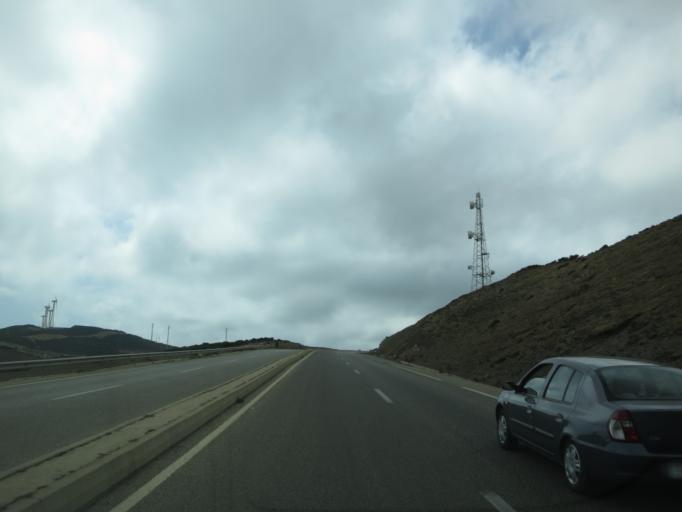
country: ES
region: Ceuta
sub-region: Ceuta
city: Ceuta
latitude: 35.8599
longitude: -5.4285
